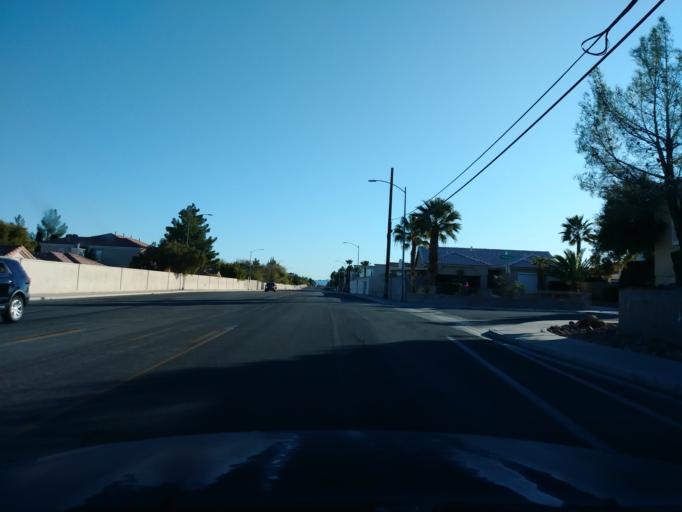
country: US
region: Nevada
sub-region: Clark County
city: Spring Valley
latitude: 36.1566
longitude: -115.2711
